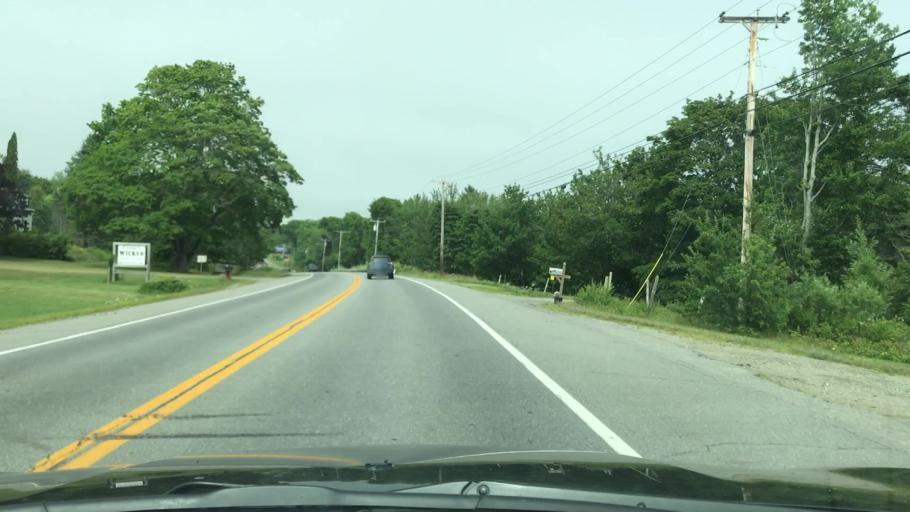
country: US
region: Maine
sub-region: Waldo County
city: Belfast
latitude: 44.4380
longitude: -68.9396
